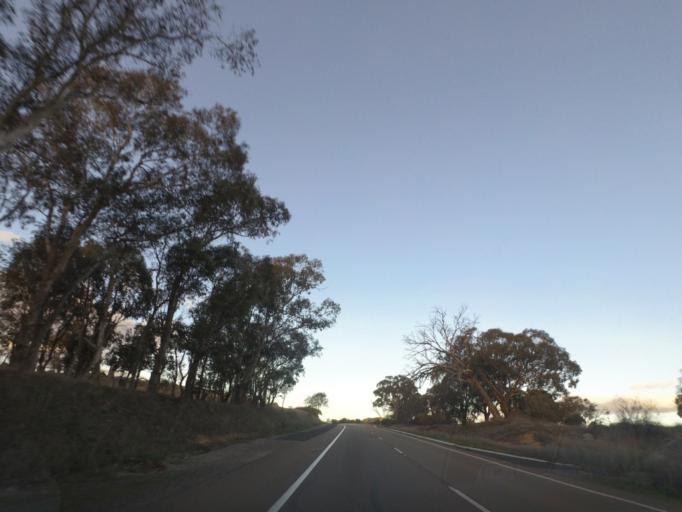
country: AU
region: New South Wales
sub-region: Yass Valley
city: Yass
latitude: -34.7696
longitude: 148.7838
